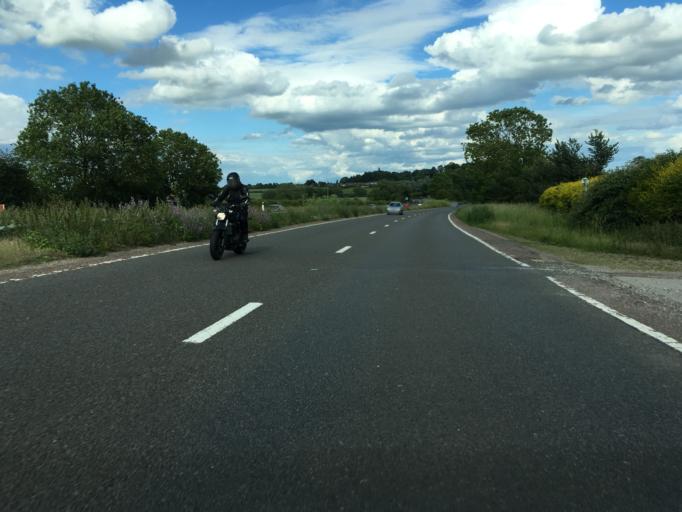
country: GB
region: England
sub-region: Oxfordshire
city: Wheatley
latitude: 51.7633
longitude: -1.1730
